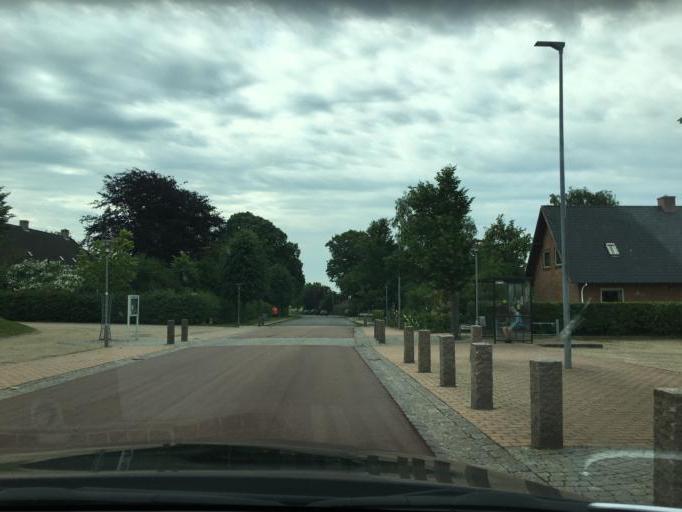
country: DK
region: South Denmark
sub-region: Kolding Kommune
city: Kolding
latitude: 55.5834
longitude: 9.4922
